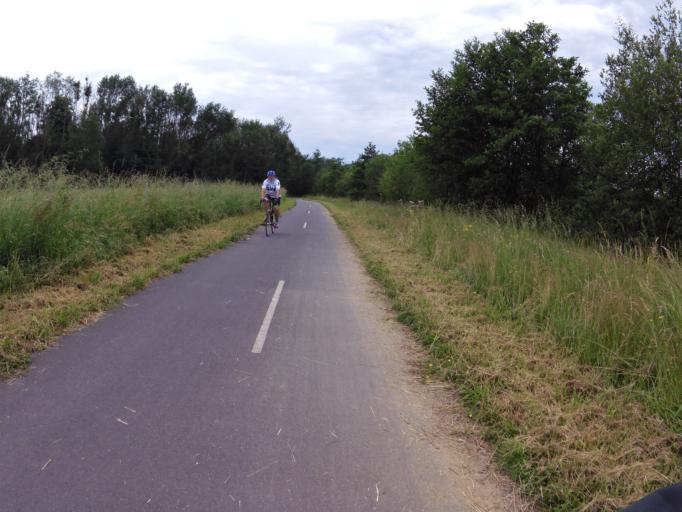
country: FR
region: Champagne-Ardenne
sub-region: Departement des Ardennes
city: Donchery
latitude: 49.7044
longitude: 4.8974
